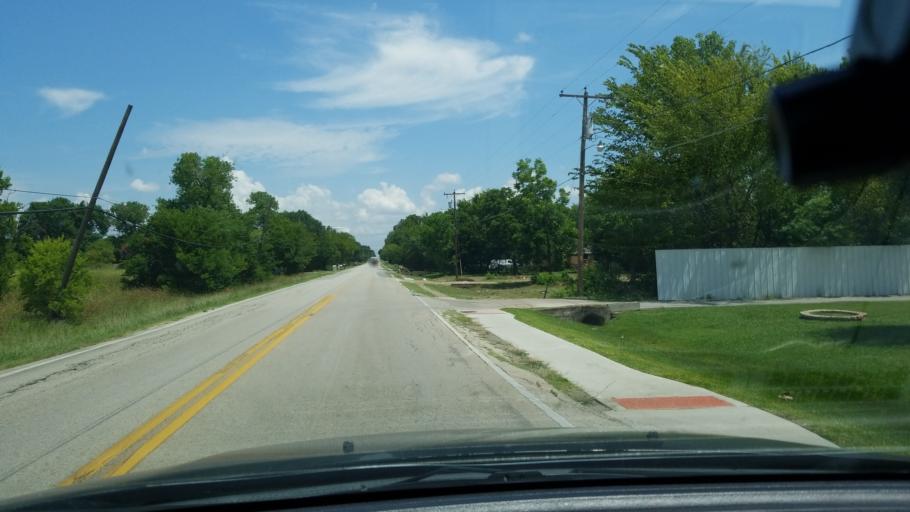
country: US
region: Texas
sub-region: Dallas County
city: Balch Springs
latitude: 32.7504
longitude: -96.6312
